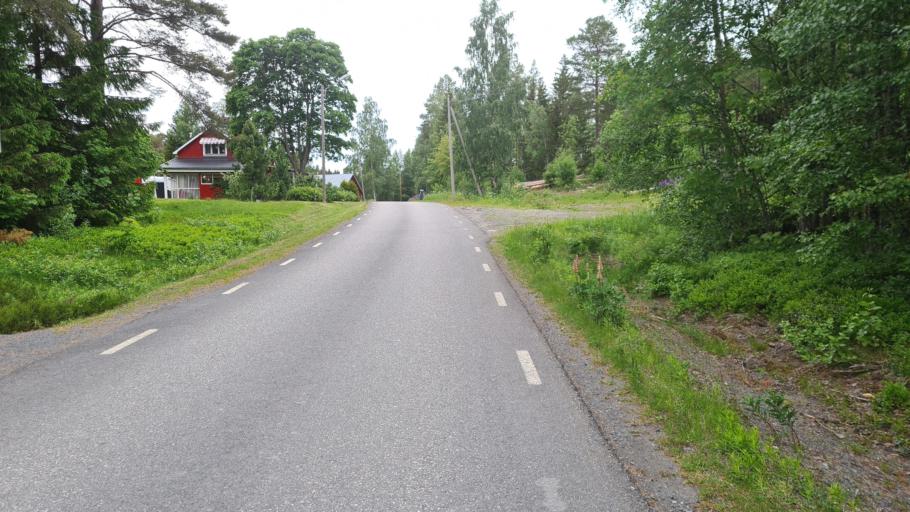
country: SE
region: Vaesternorrland
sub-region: Kramfors Kommun
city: Nordingra
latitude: 62.9734
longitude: 18.4251
